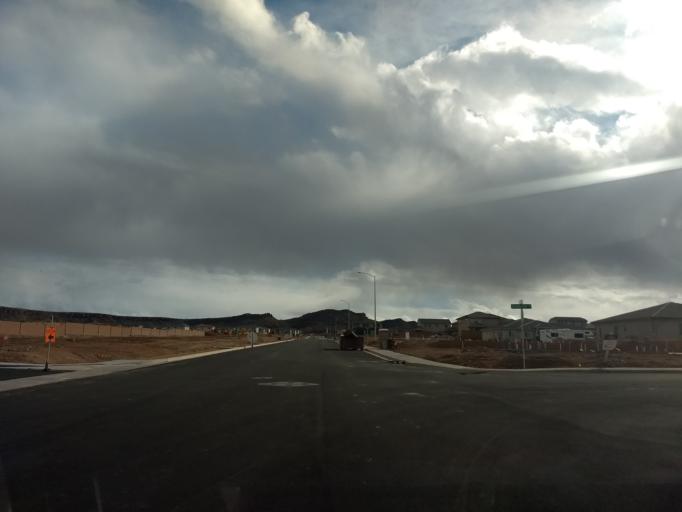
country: US
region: Utah
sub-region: Washington County
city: Washington
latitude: 37.0615
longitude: -113.5176
